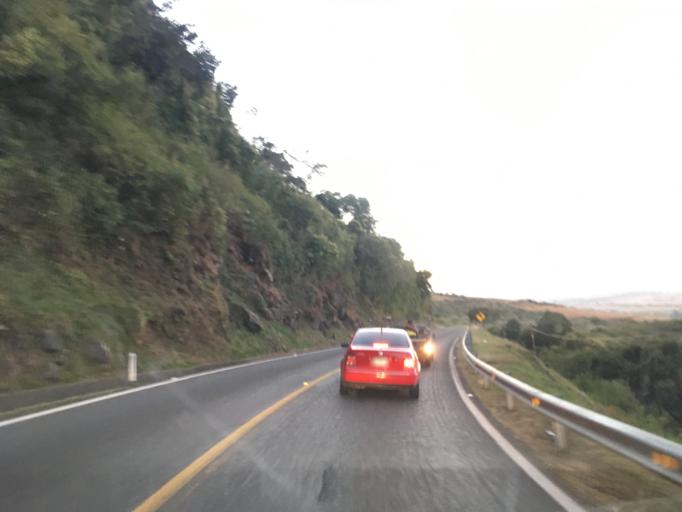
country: MX
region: Michoacan
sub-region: Zinapecuaro
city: Santa Clara del Tule
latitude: 19.8107
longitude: -100.8183
